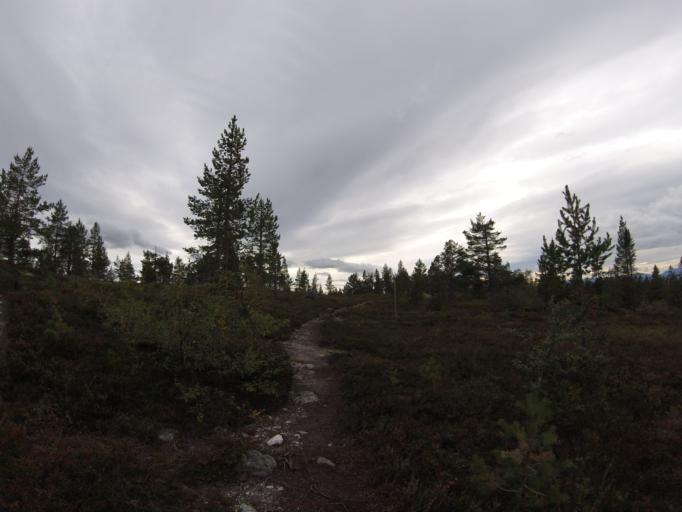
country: NO
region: Buskerud
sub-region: Flesberg
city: Lampeland
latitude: 59.7455
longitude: 9.4197
